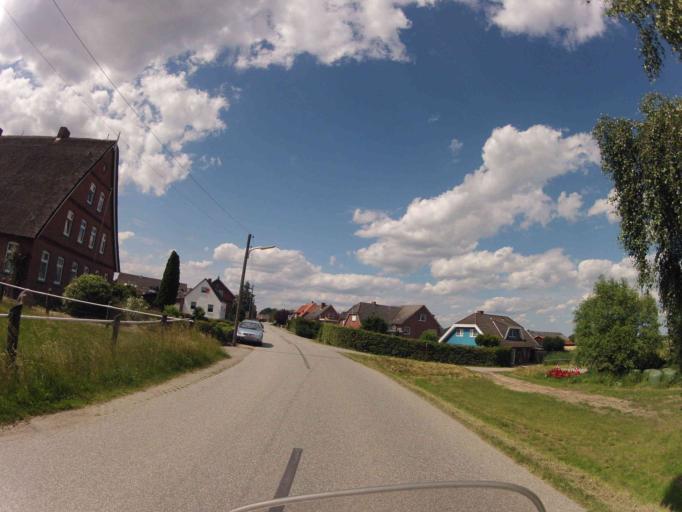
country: DE
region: Hamburg
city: Bergedorf
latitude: 53.4402
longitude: 10.1847
